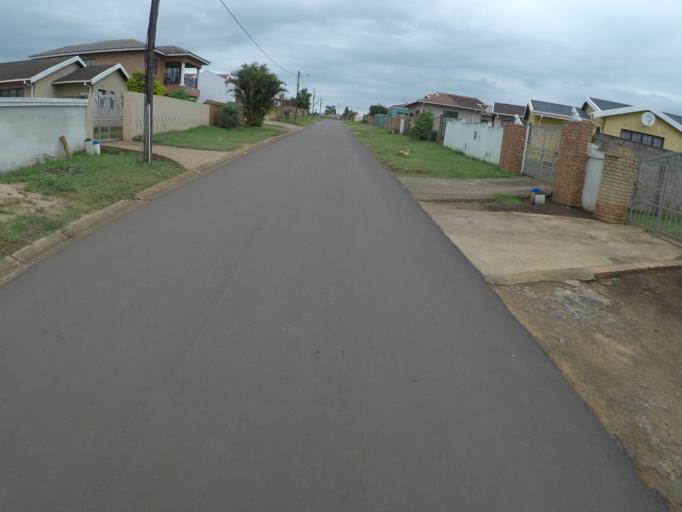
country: ZA
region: KwaZulu-Natal
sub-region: uThungulu District Municipality
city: Empangeni
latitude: -28.7749
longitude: 31.8490
